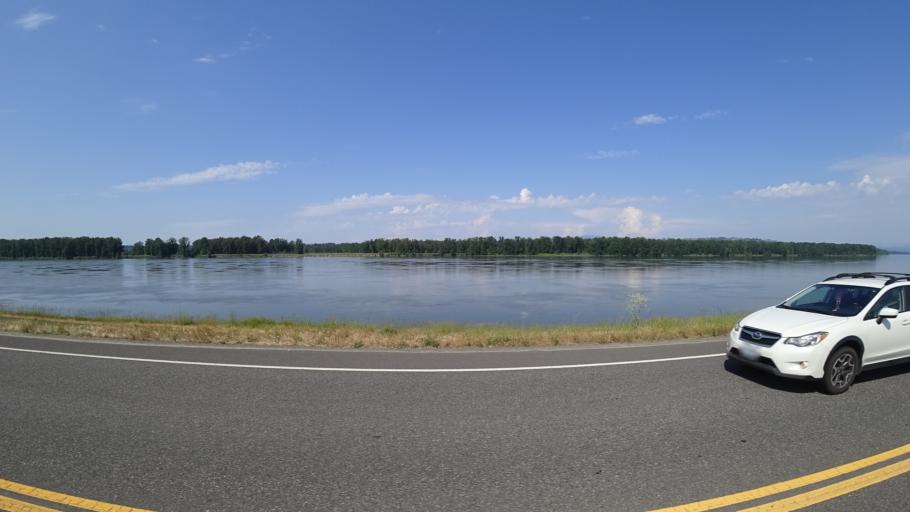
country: US
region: Washington
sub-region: Clark County
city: Mill Plain
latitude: 45.5640
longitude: -122.5139
